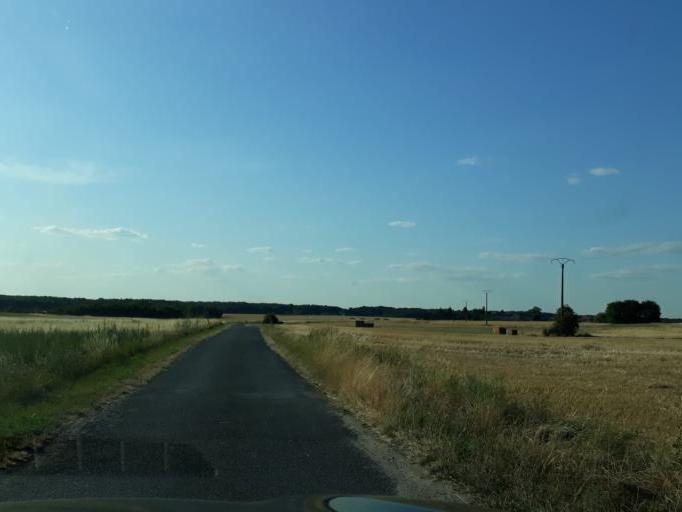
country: FR
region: Centre
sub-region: Departement du Loiret
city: Chaingy
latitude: 47.8950
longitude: 1.7628
